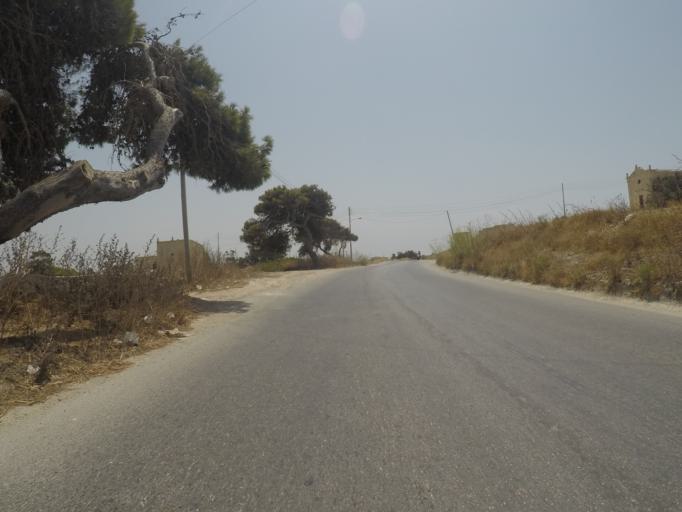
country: MT
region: Is-Siggiewi
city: Siggiewi
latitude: 35.8670
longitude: 14.4167
